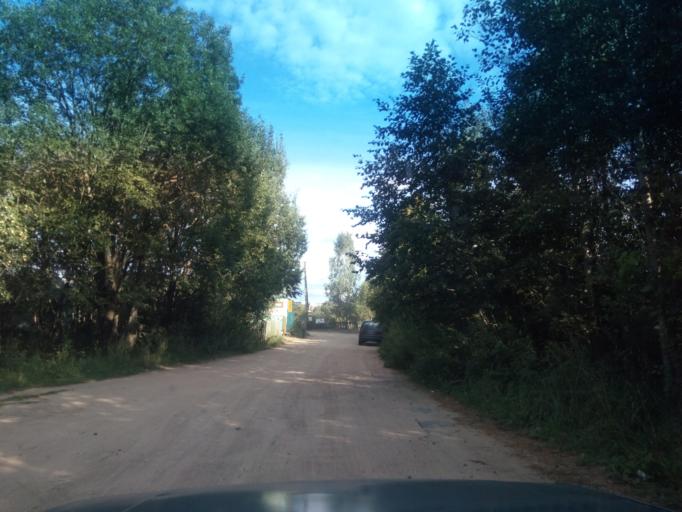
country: BY
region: Vitebsk
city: Polatsk
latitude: 55.4075
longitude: 28.7571
